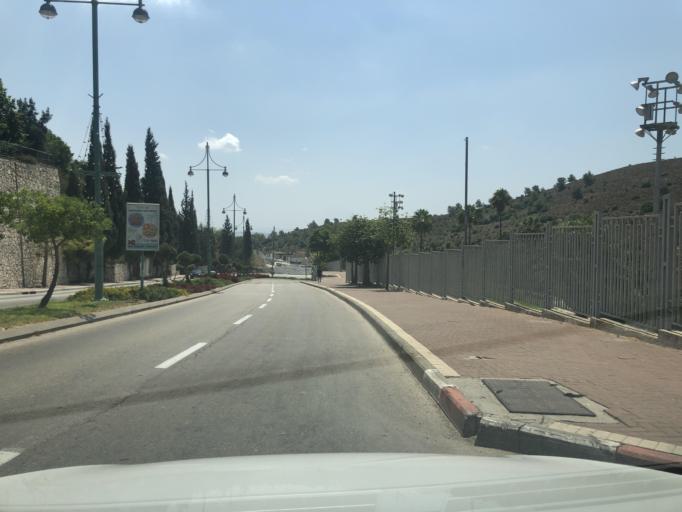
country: IL
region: Haifa
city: Daliyat el Karmil
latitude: 32.6534
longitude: 35.1058
